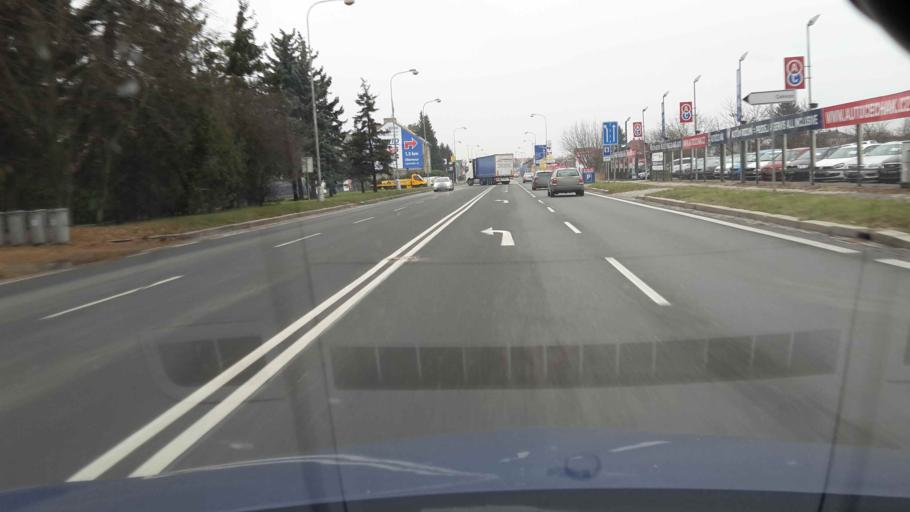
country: CZ
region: Olomoucky
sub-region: Okres Olomouc
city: Olomouc
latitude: 49.5847
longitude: 17.2918
